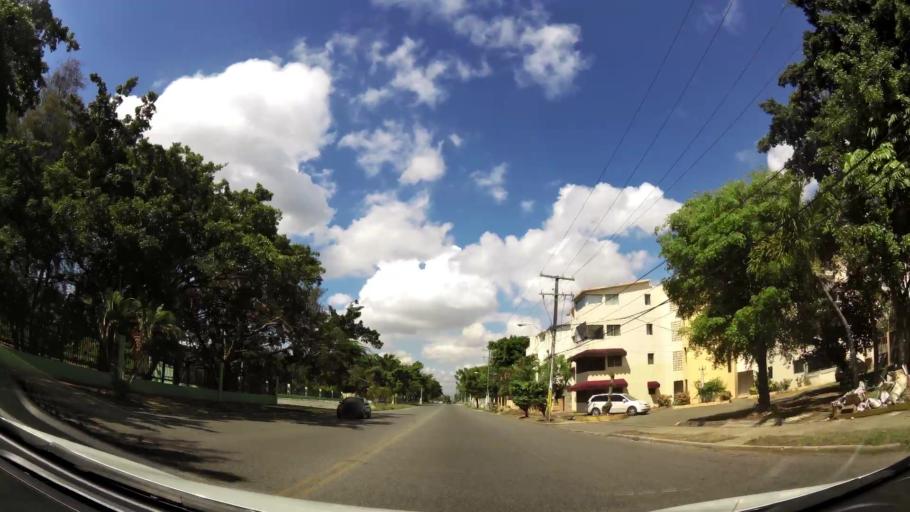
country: DO
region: Santo Domingo
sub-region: Santo Domingo
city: Santo Domingo Este
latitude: 18.4804
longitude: -69.8594
